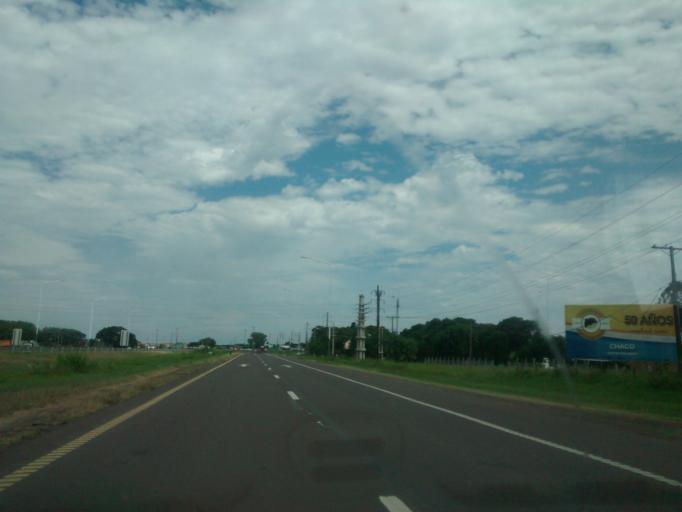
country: AR
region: Chaco
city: Fontana
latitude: -27.4084
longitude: -59.0065
